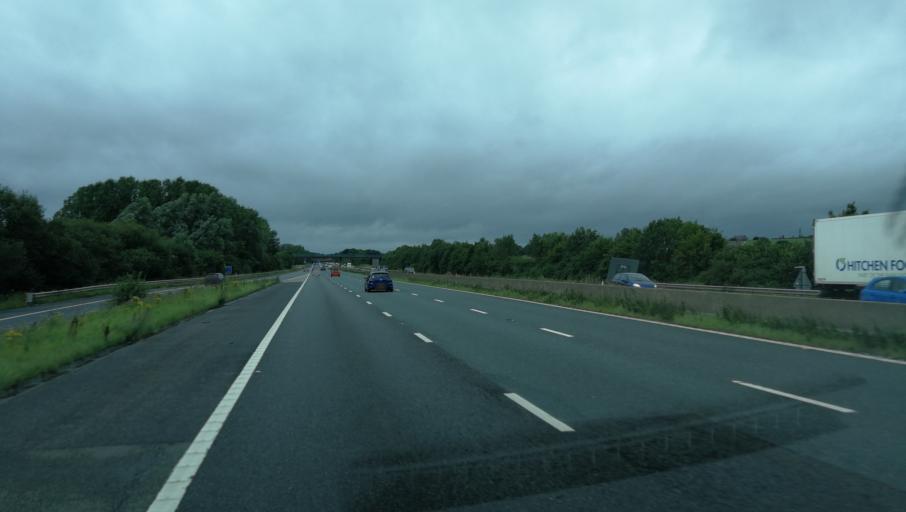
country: GB
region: England
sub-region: Borough of Wigan
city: Tyldesley
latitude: 53.5453
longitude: -2.4521
